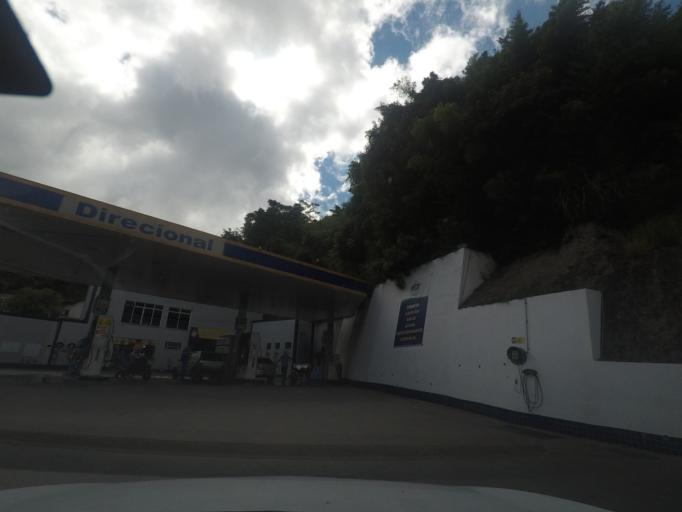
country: BR
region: Rio de Janeiro
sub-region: Teresopolis
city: Teresopolis
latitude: -22.4002
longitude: -42.9621
